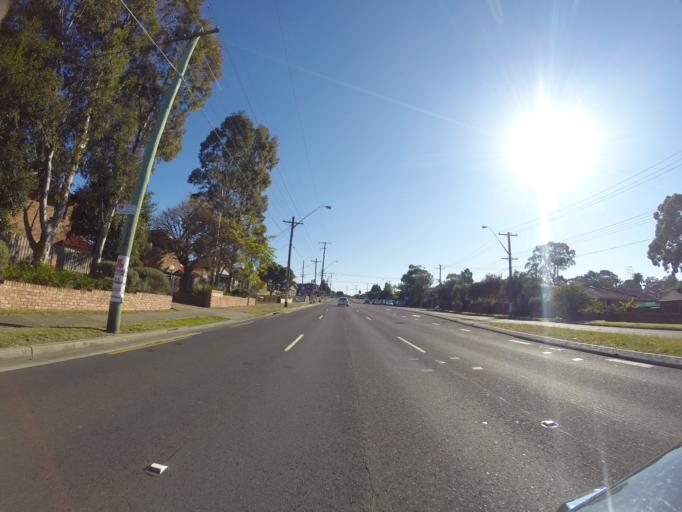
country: AU
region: New South Wales
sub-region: Kogarah
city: Blakehurst
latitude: -33.9841
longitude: 151.1093
